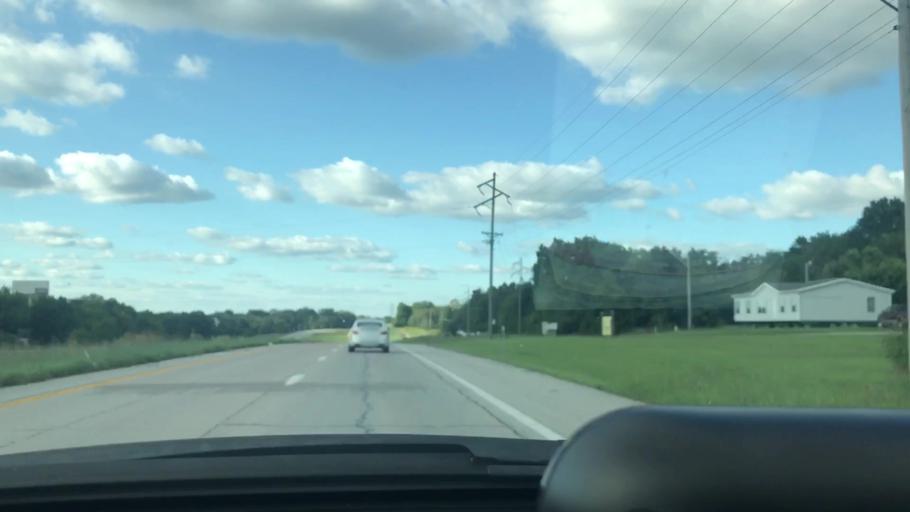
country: US
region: Missouri
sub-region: Pettis County
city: Sedalia
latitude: 38.6290
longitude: -93.2672
